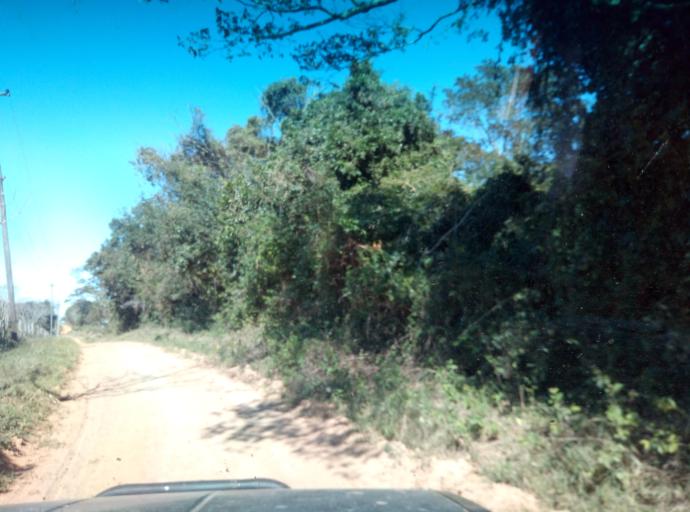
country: PY
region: Caaguazu
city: Doctor Cecilio Baez
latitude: -25.1739
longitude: -56.2020
